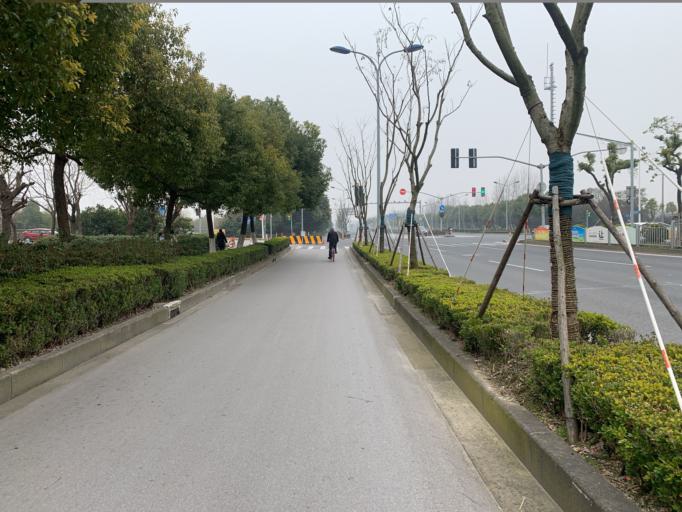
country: CN
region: Shanghai Shi
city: Huamu
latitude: 31.2419
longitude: 121.6212
